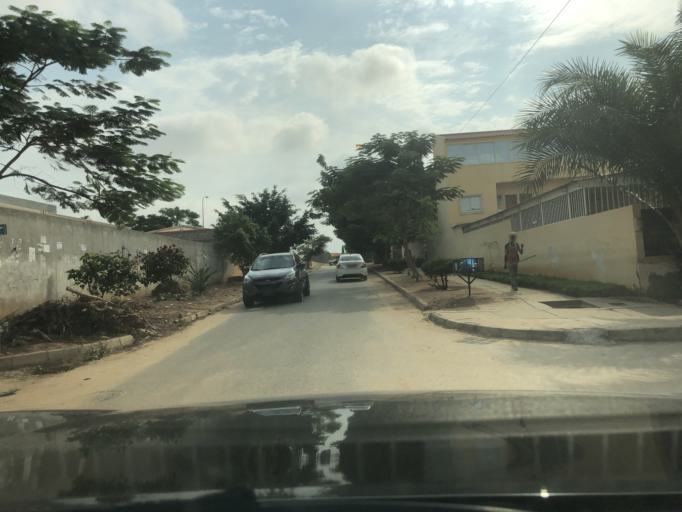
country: AO
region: Luanda
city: Luanda
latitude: -8.9363
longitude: 13.2462
